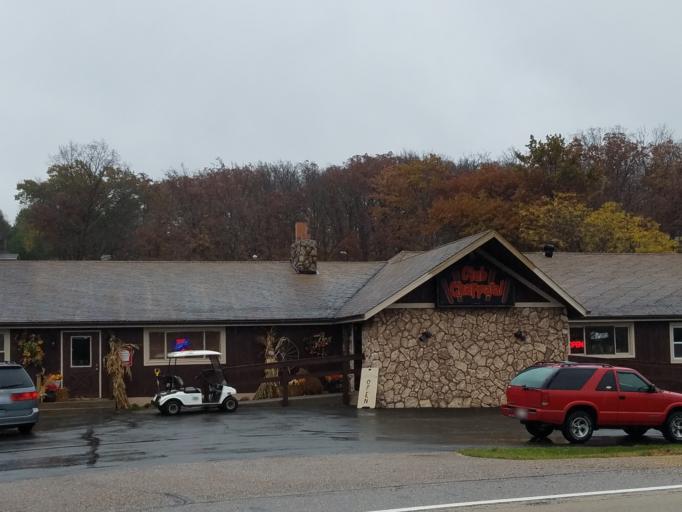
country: US
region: Wisconsin
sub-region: Juneau County
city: Elroy
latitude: 43.6338
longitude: -90.1756
